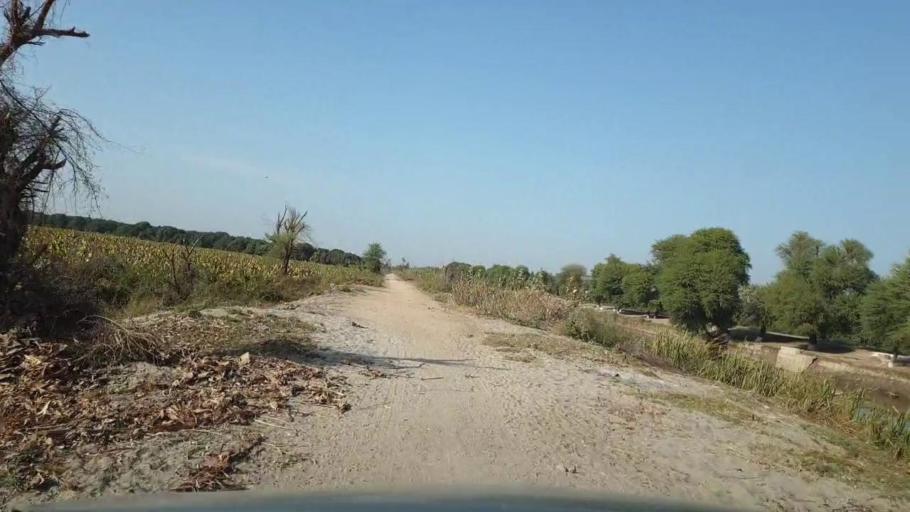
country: PK
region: Sindh
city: Tando Adam
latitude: 25.6017
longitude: 68.6254
